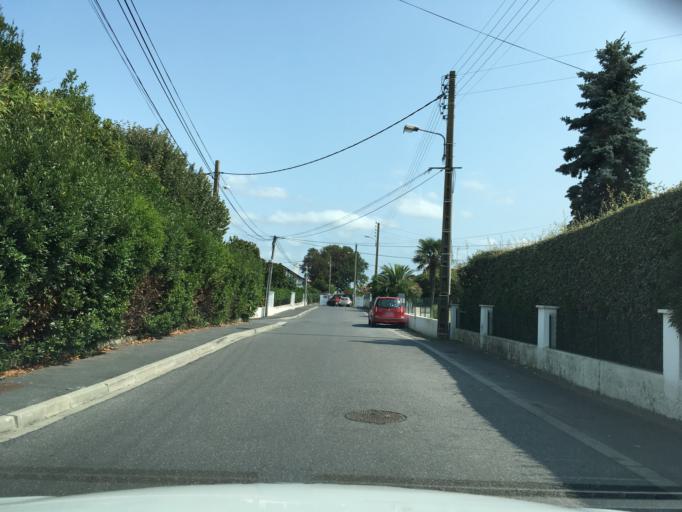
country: FR
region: Aquitaine
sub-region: Departement des Pyrenees-Atlantiques
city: Anglet
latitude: 43.4922
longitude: -1.5302
